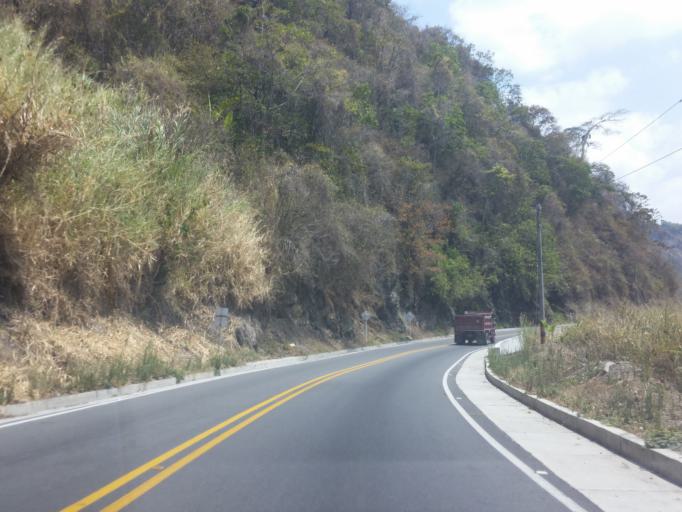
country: CO
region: Caldas
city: Chinchina
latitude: 4.9928
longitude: -75.5760
